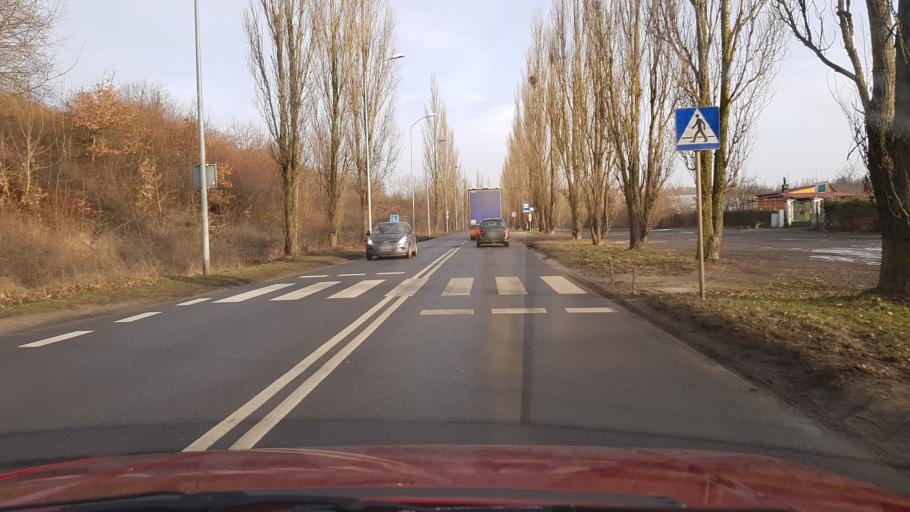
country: PL
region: West Pomeranian Voivodeship
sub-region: Szczecin
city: Szczecin
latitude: 53.4676
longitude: 14.5790
